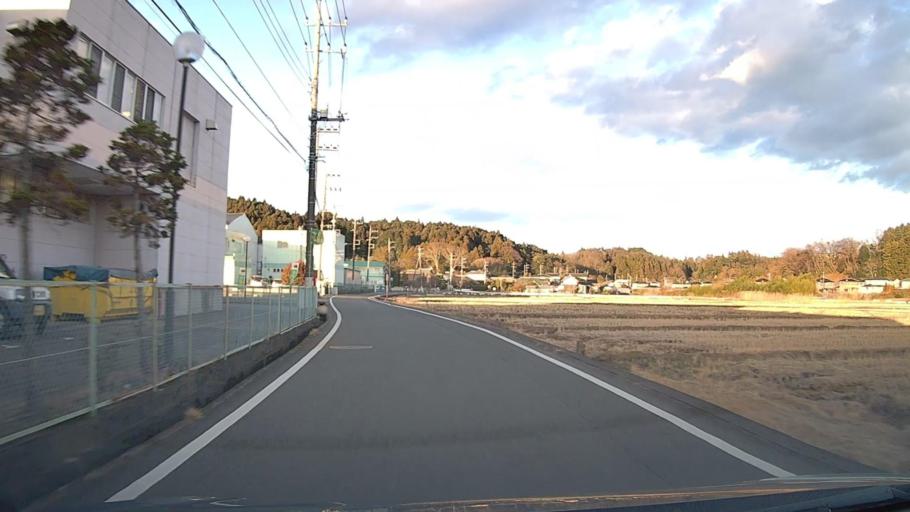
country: JP
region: Ibaraki
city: Kitaibaraki
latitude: 36.8514
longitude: 140.7763
